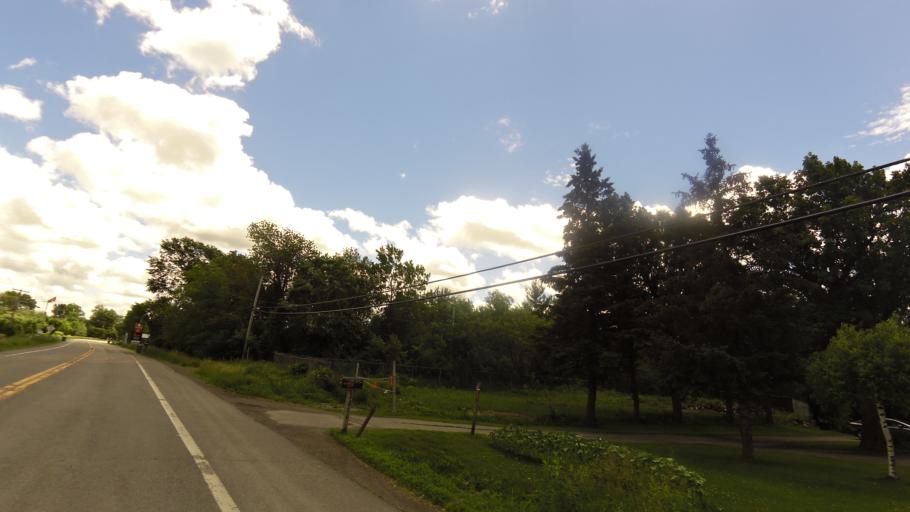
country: CA
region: Quebec
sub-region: Monteregie
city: Hudson
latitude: 45.4948
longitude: -74.1375
